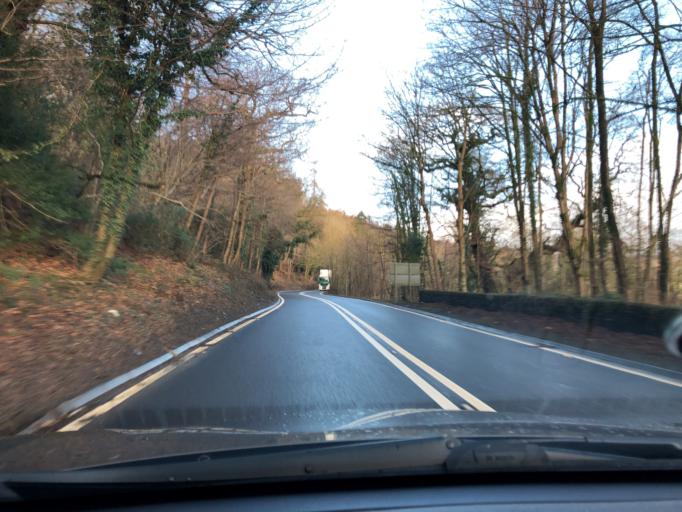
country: GB
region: England
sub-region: Cumbria
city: Ulverston
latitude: 54.2428
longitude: -3.0483
